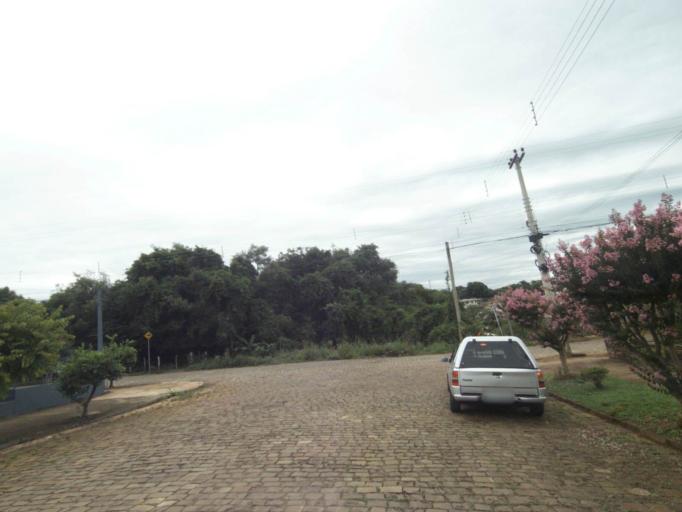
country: BR
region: Rio Grande do Sul
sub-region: Lagoa Vermelha
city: Lagoa Vermelha
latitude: -28.2136
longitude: -51.5293
